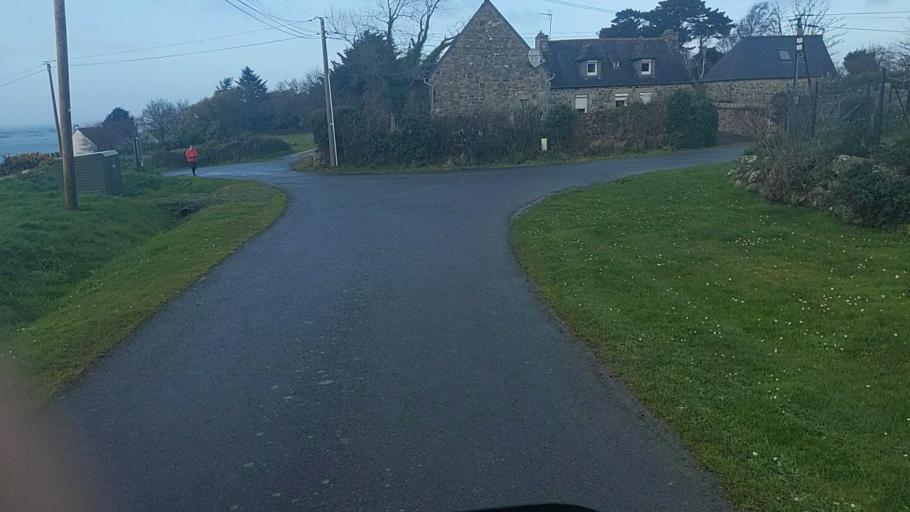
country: FR
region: Brittany
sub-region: Departement des Cotes-d'Armor
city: Plougrescant
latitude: 48.8330
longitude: -3.1880
